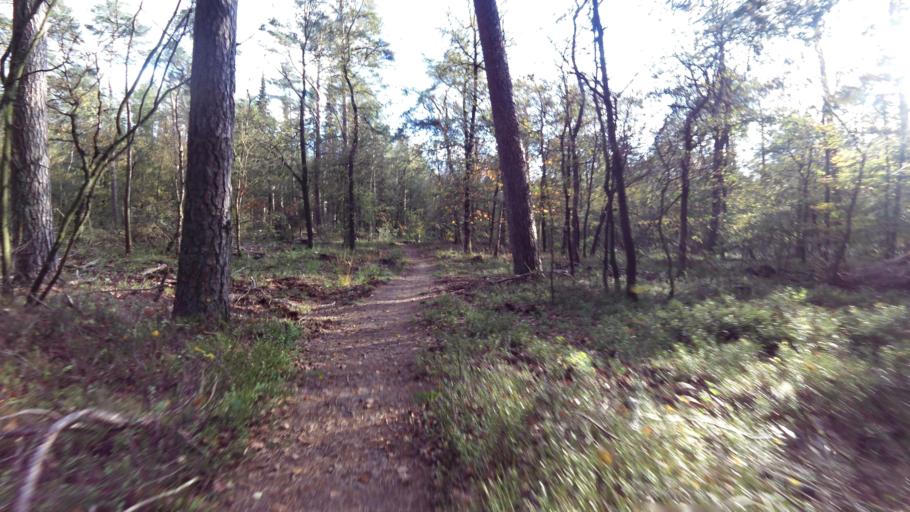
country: NL
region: Gelderland
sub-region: Gemeente Nunspeet
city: Nunspeet
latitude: 52.3405
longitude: 5.8366
